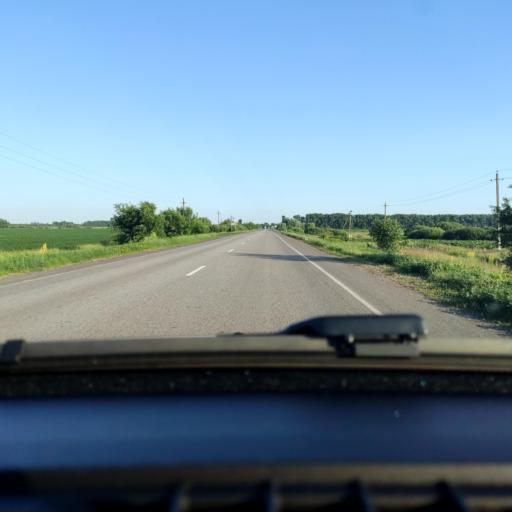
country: RU
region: Voronezj
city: Kashirskoye
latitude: 51.4749
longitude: 39.8603
